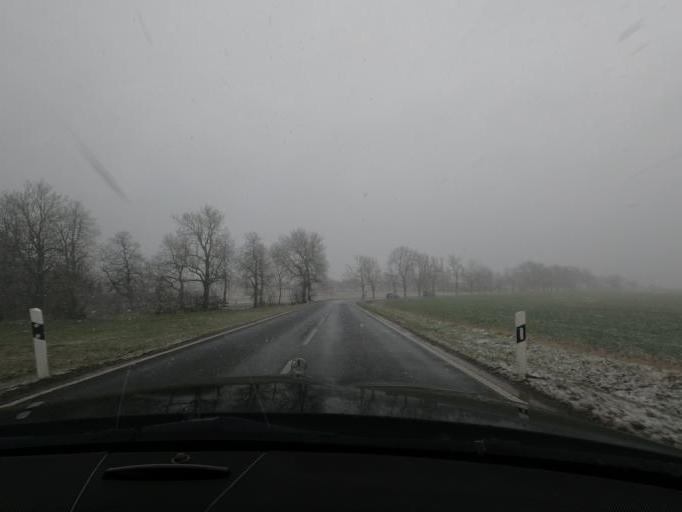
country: DE
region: Thuringia
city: Kullstedt
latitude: 51.2692
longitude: 10.2745
